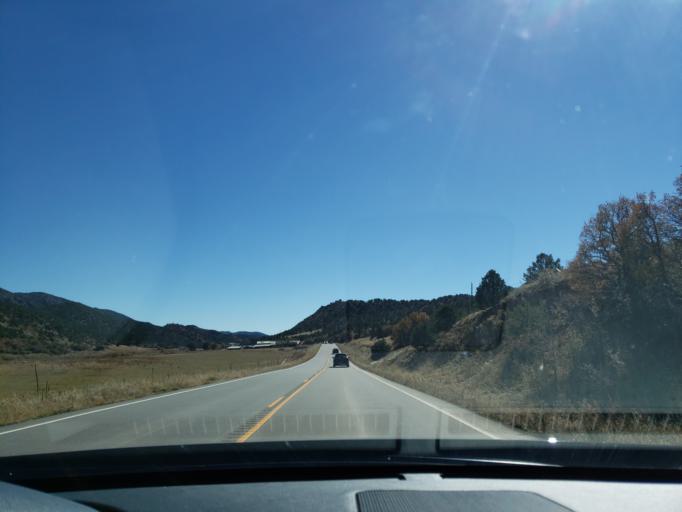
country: US
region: Colorado
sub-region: Fremont County
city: Canon City
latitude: 38.6081
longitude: -105.4384
